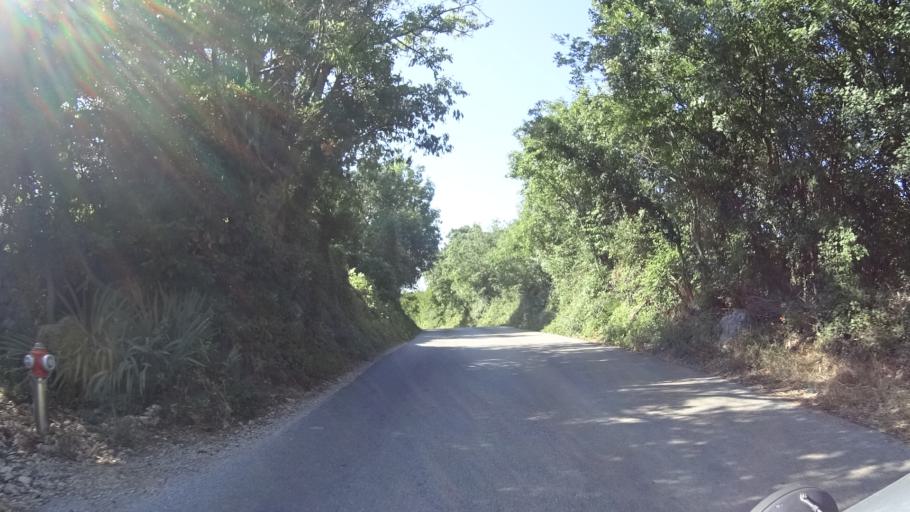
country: HR
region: Istarska
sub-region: Grad Labin
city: Rabac
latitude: 45.0162
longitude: 14.1503
